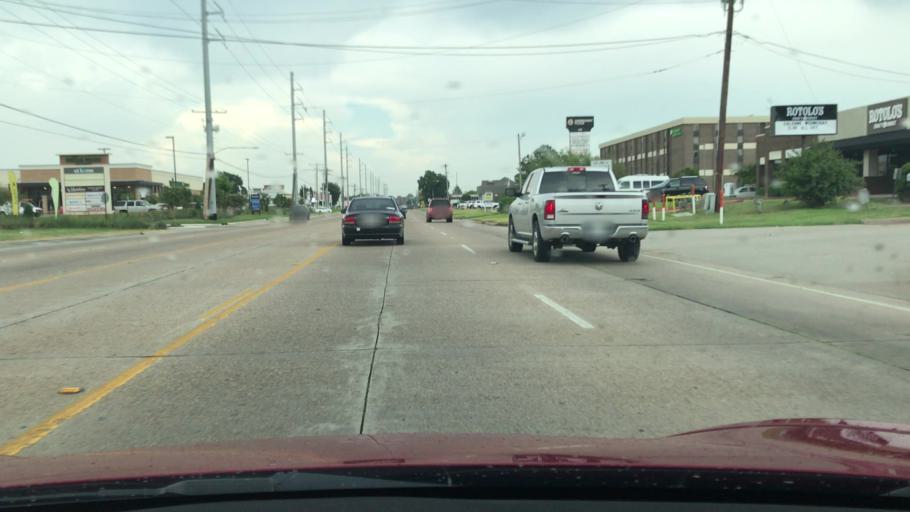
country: US
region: Louisiana
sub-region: Bossier Parish
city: Bossier City
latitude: 32.4434
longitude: -93.7288
